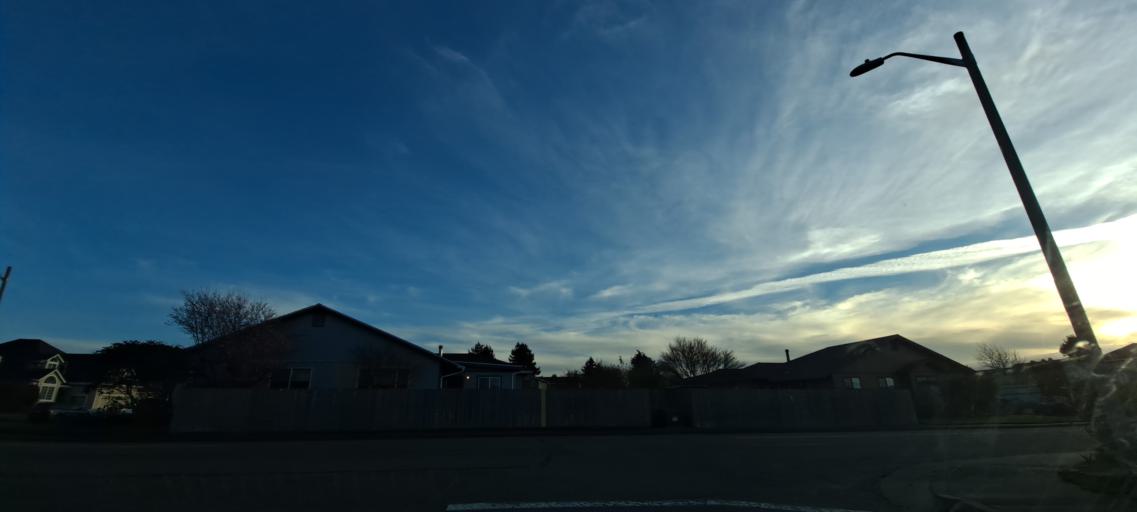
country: US
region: California
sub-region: Humboldt County
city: Fortuna
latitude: 40.5779
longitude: -124.1328
